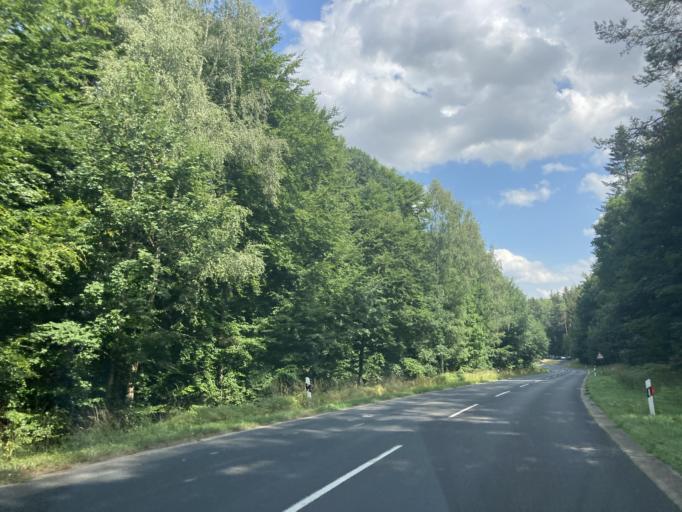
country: DE
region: Hesse
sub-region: Regierungsbezirk Kassel
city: Grossenluder
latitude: 50.5426
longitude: 9.5450
